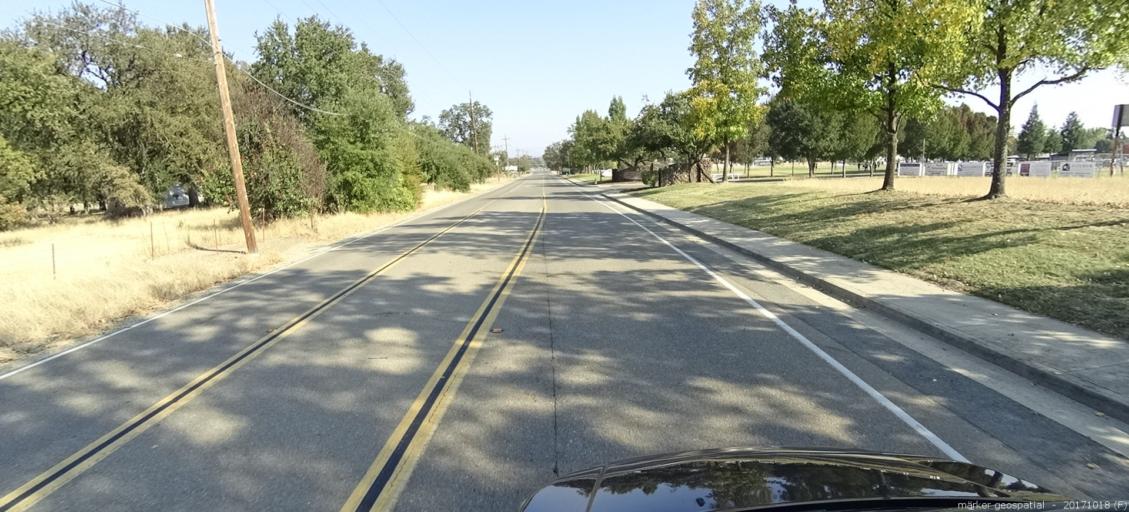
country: US
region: California
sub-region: Shasta County
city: Palo Cedro
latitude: 40.5637
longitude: -122.2443
